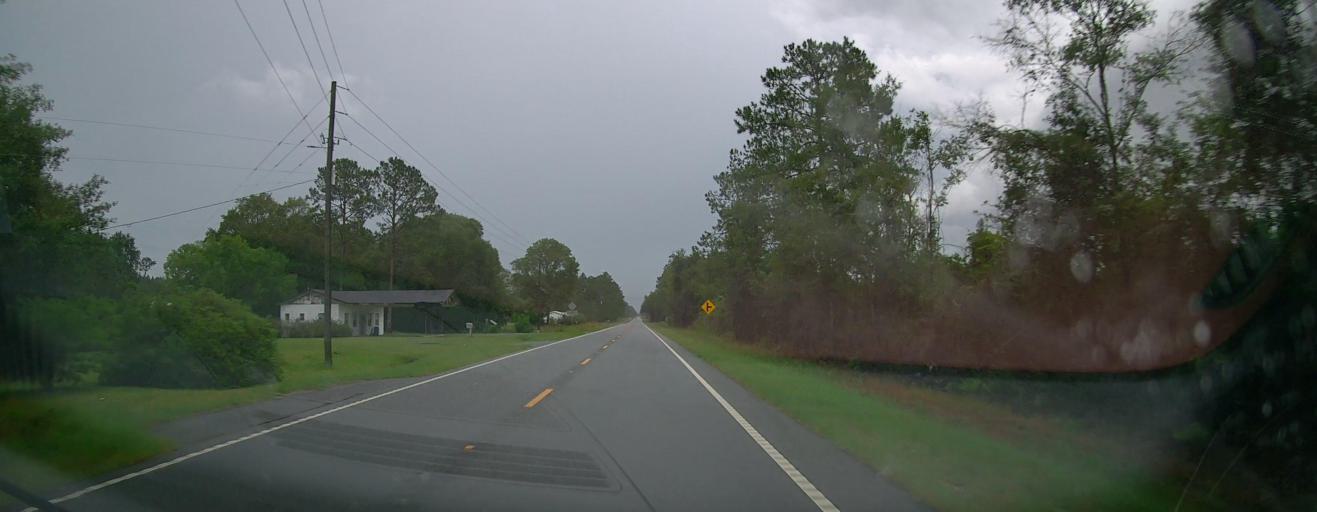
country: US
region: Georgia
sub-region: Brantley County
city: Nahunta
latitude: 31.3399
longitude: -81.9754
